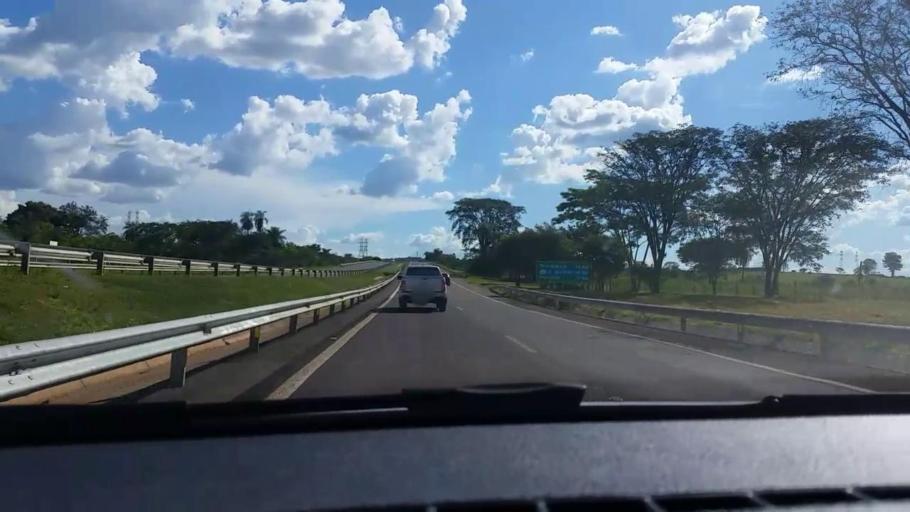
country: BR
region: Sao Paulo
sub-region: Bauru
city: Bauru
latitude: -22.4067
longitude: -49.0976
